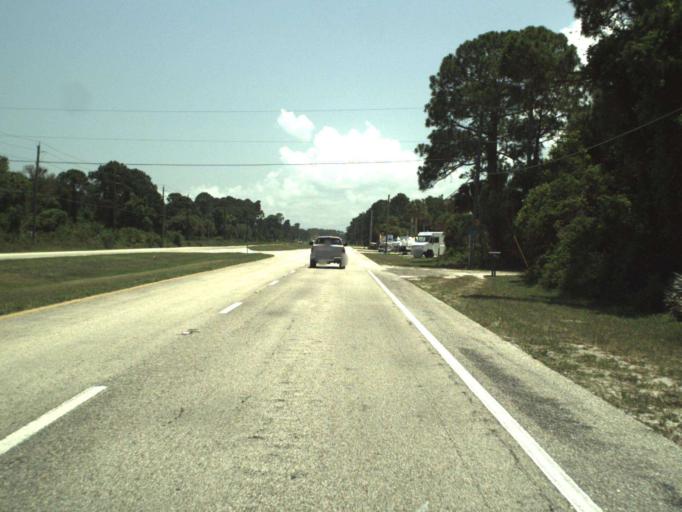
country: US
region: Florida
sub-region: Volusia County
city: Oak Hill
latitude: 28.8896
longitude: -80.8592
